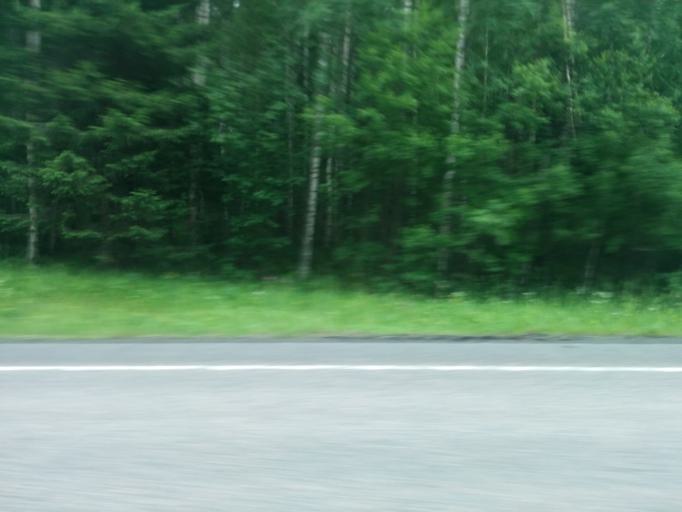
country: FI
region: Pirkanmaa
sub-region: Tampere
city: Orivesi
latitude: 61.7050
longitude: 24.4458
